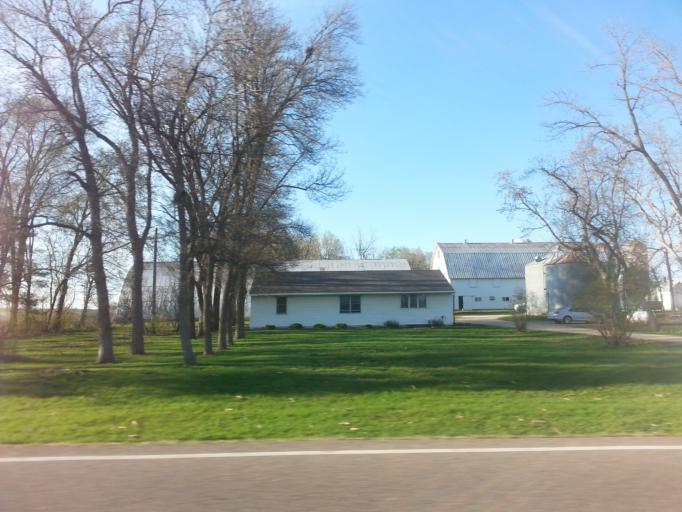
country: US
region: Minnesota
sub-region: Goodhue County
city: Cannon Falls
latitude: 44.5435
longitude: -93.0307
